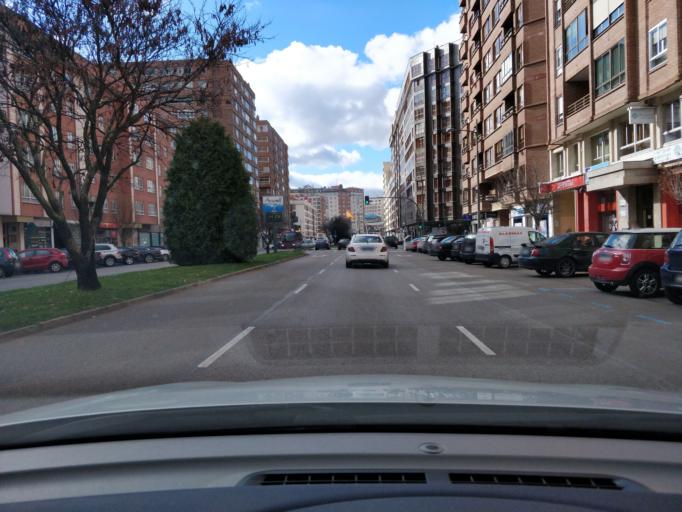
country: ES
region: Castille and Leon
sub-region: Provincia de Burgos
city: Burgos
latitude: 42.3449
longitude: -3.6930
